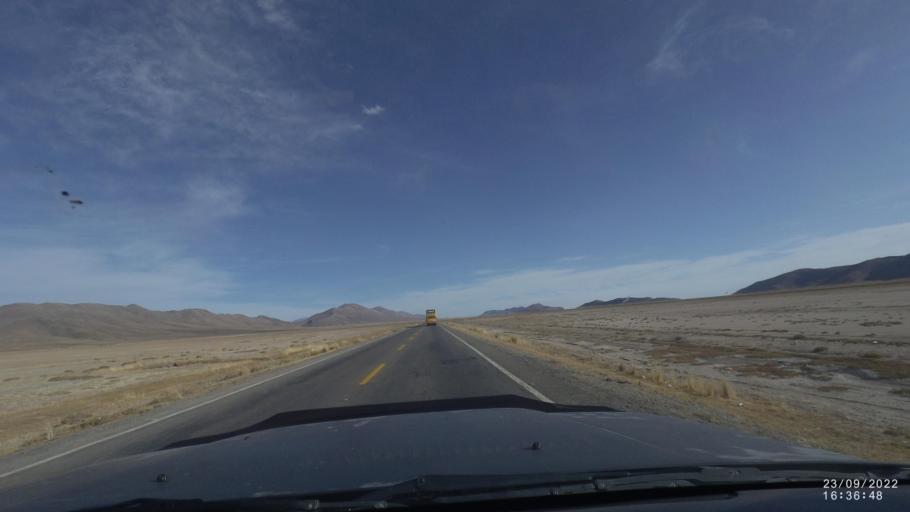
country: BO
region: Oruro
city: Machacamarca
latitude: -18.2256
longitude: -67.0068
